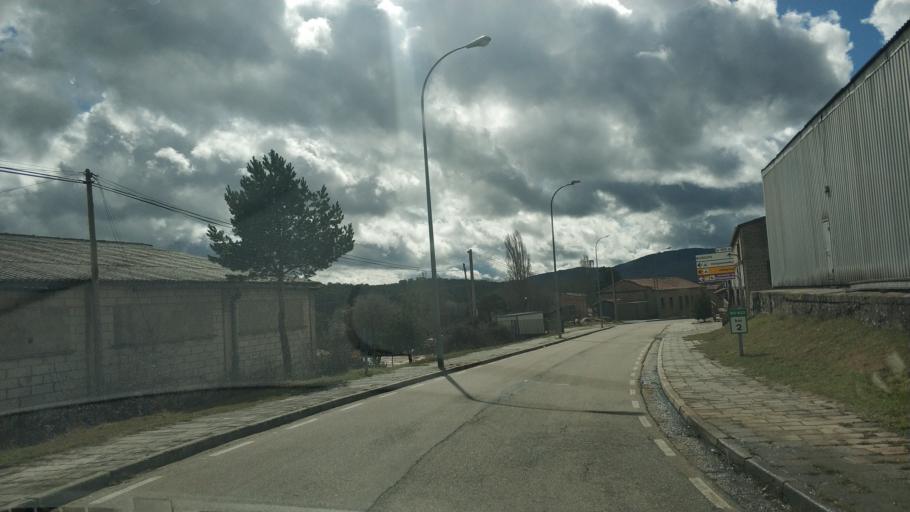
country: ES
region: Castille and Leon
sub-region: Provincia de Burgos
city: Quintanar de la Sierra
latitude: 41.9870
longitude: -3.0290
